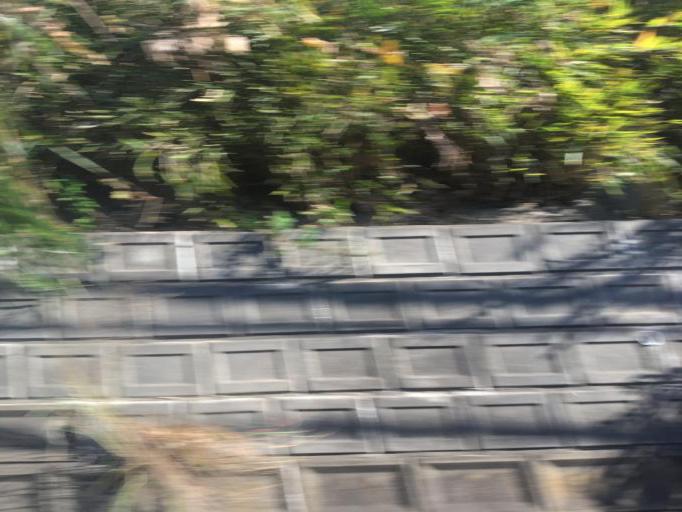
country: JP
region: Chiba
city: Funabashi
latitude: 35.7131
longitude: 139.9567
